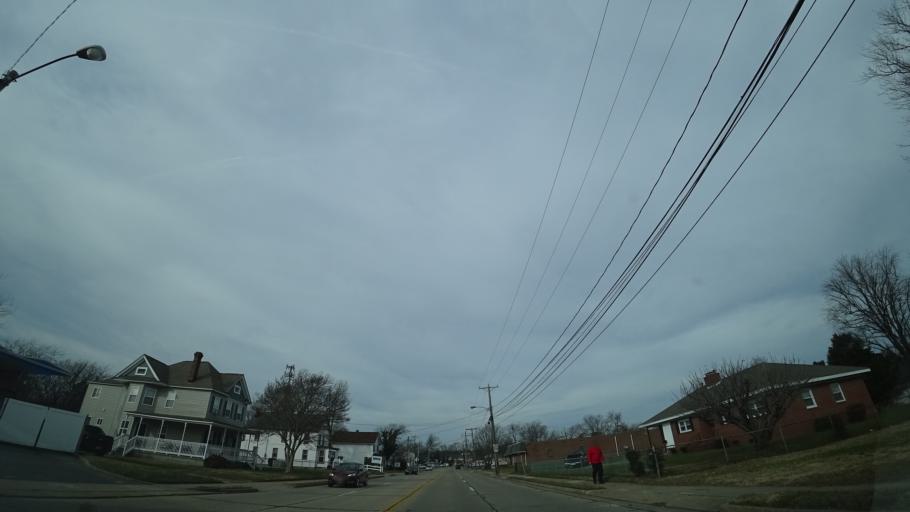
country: US
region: Virginia
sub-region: City of Hampton
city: East Hampton
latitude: 37.0224
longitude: -76.3197
